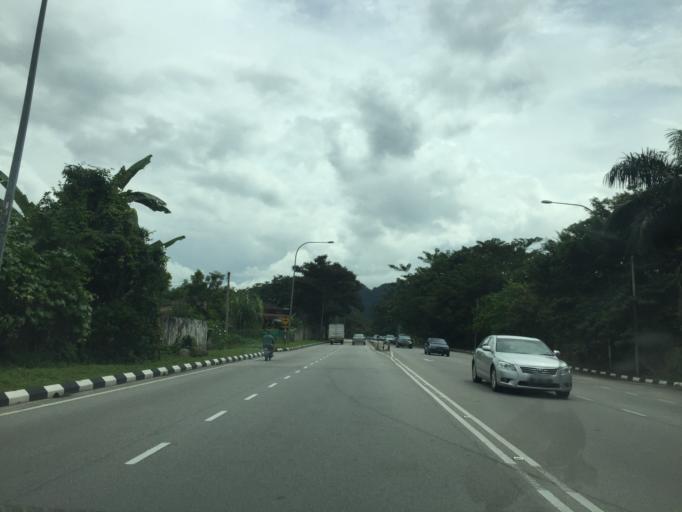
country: MY
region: Perak
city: Ipoh
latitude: 4.5683
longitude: 101.1176
